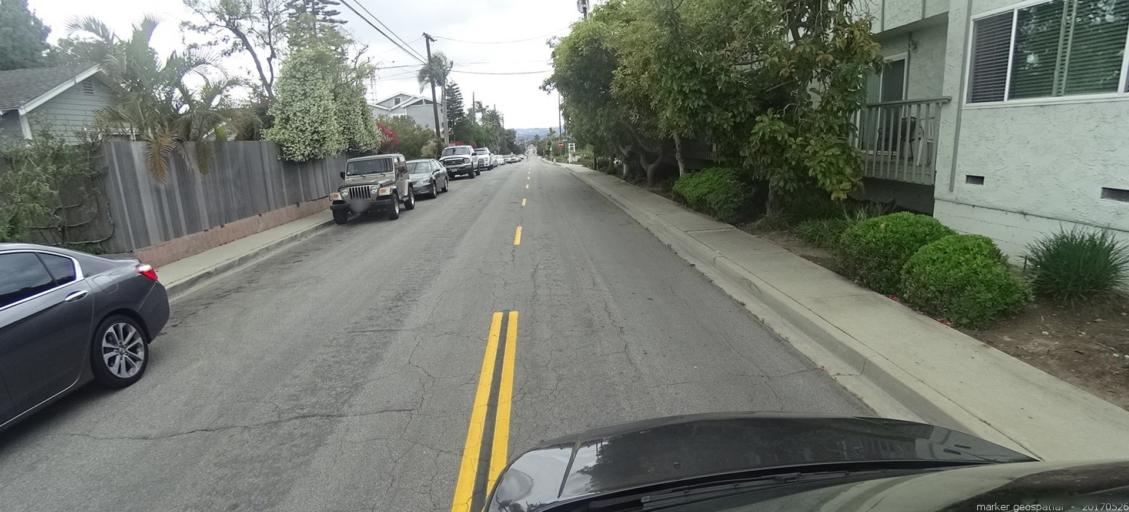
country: US
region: California
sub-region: Los Angeles County
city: Lawndale
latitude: 33.8794
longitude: -118.3665
